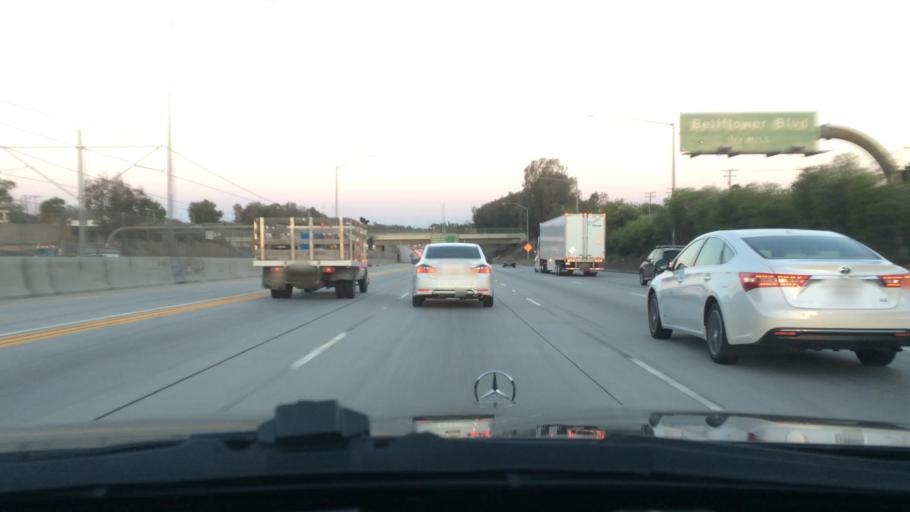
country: US
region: California
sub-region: Los Angeles County
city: Downey
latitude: 33.9140
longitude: -118.1137
